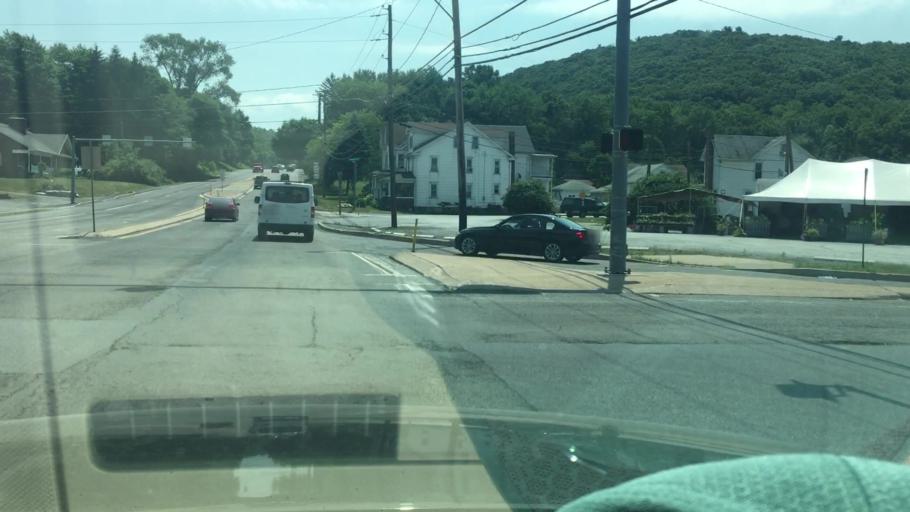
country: US
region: Pennsylvania
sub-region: Schuylkill County
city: Tamaqua
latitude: 40.7584
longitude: -75.9451
